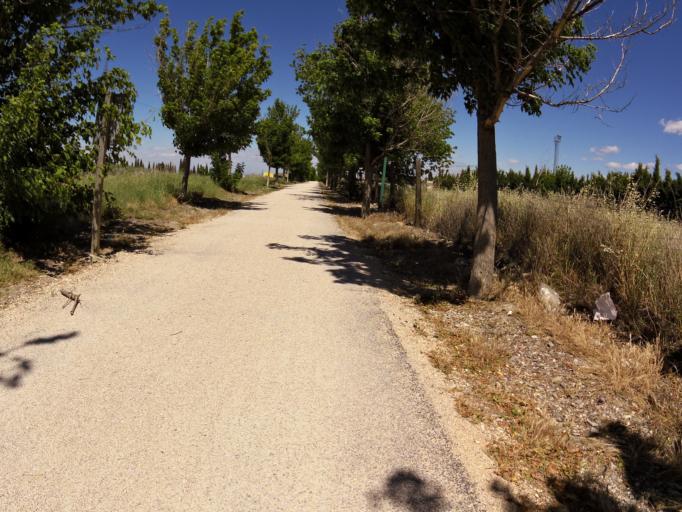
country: ES
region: Andalusia
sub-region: Provincia de Jaen
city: Torre del Campo
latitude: 37.7753
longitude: -3.9019
